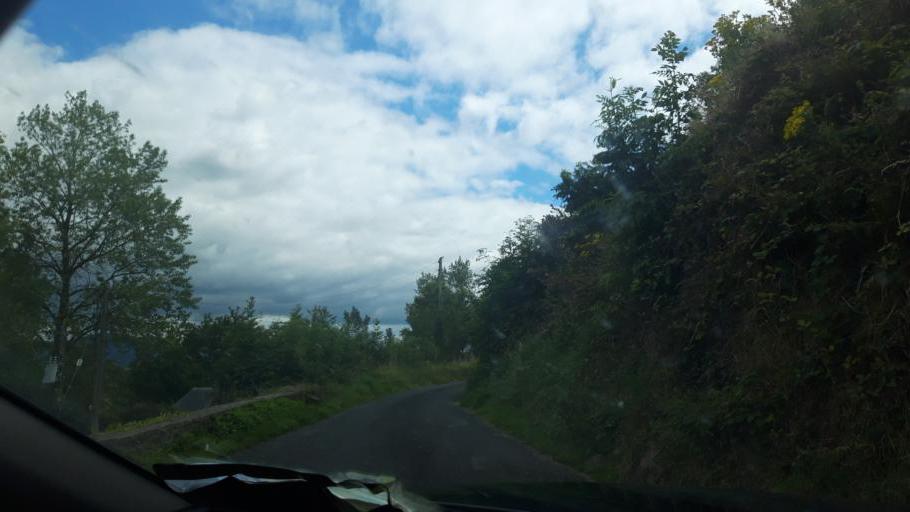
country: IE
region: Munster
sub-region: South Tipperary
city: Cluain Meala
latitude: 52.3471
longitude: -7.7006
